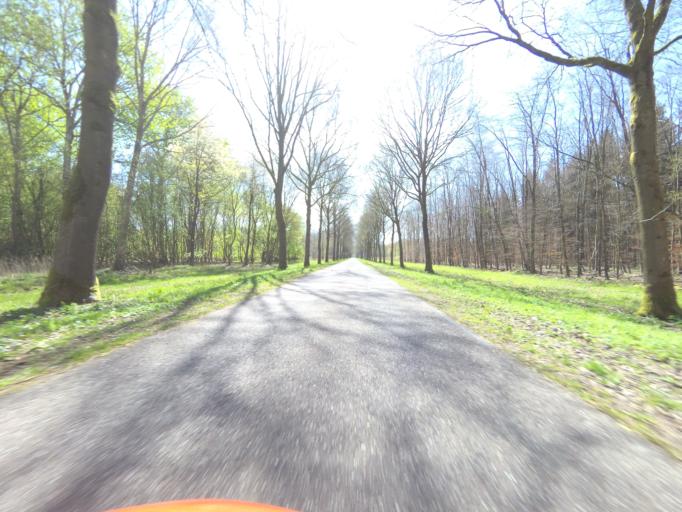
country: NL
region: Flevoland
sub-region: Gemeente Zeewolde
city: Zeewolde
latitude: 52.3107
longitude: 5.5064
